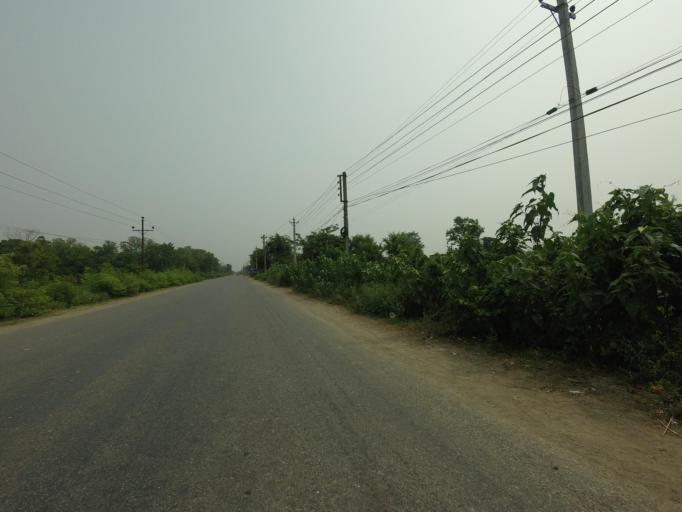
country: IN
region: Uttar Pradesh
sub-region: Maharajganj
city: Nautanwa
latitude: 27.4946
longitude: 83.2844
